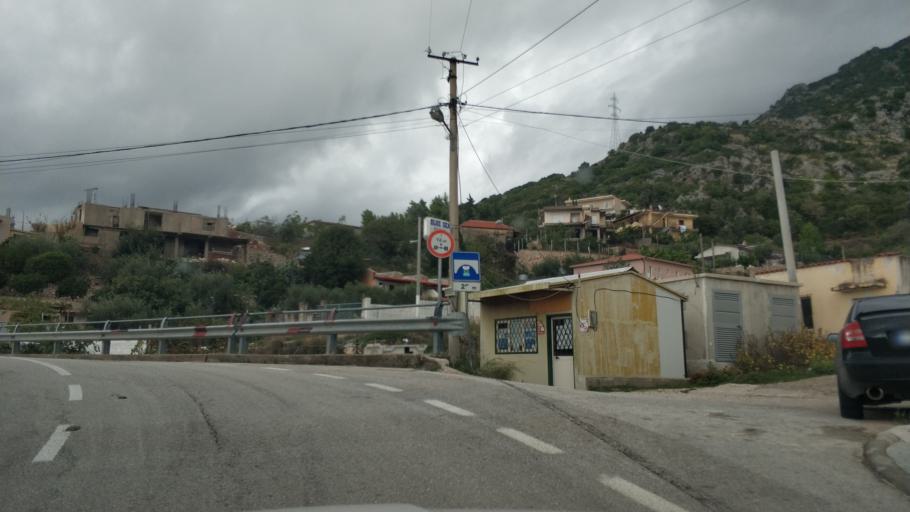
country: AL
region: Vlore
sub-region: Rrethi i Vlores
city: Vranisht
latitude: 40.1563
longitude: 19.6331
